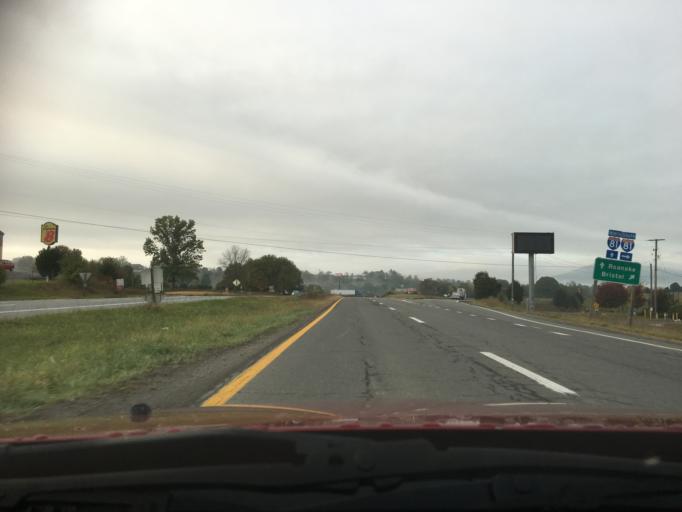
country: US
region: Virginia
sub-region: Pulaski County
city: Dublin
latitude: 37.0822
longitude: -80.6907
